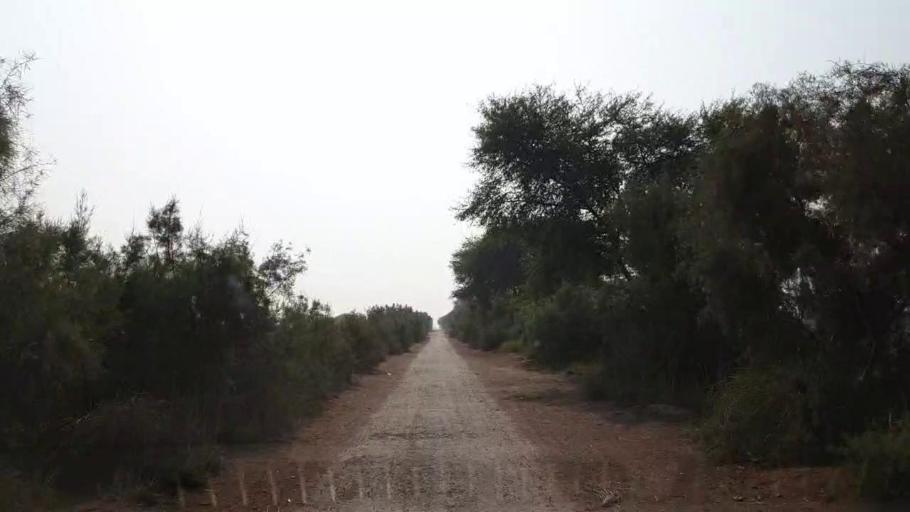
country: PK
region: Sindh
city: Bhan
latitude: 26.4677
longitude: 67.7390
